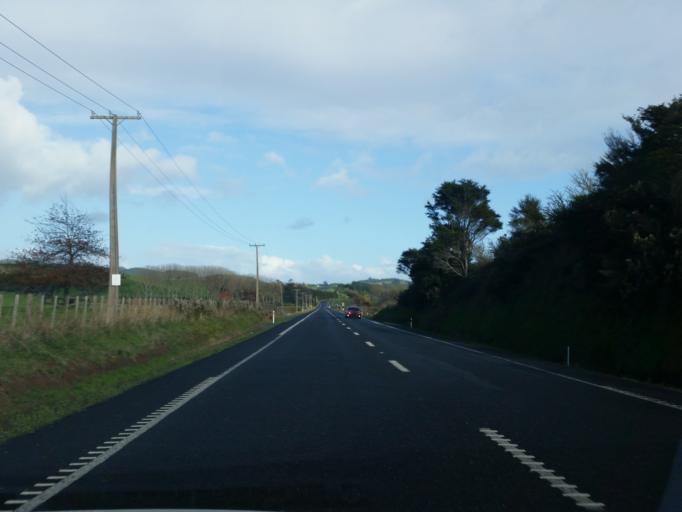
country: NZ
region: Waikato
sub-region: Hauraki District
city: Ngatea
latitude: -37.2848
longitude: 175.3956
